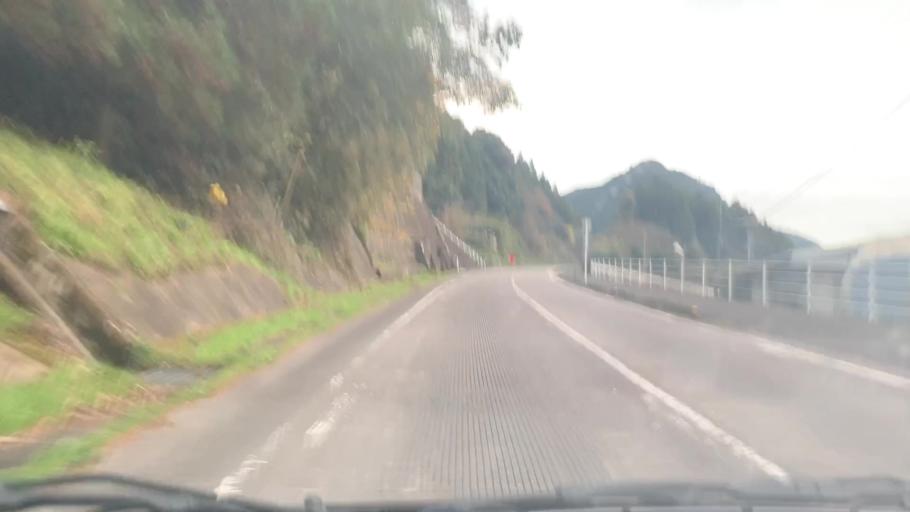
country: JP
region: Saga Prefecture
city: Kashima
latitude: 33.0561
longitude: 130.0714
